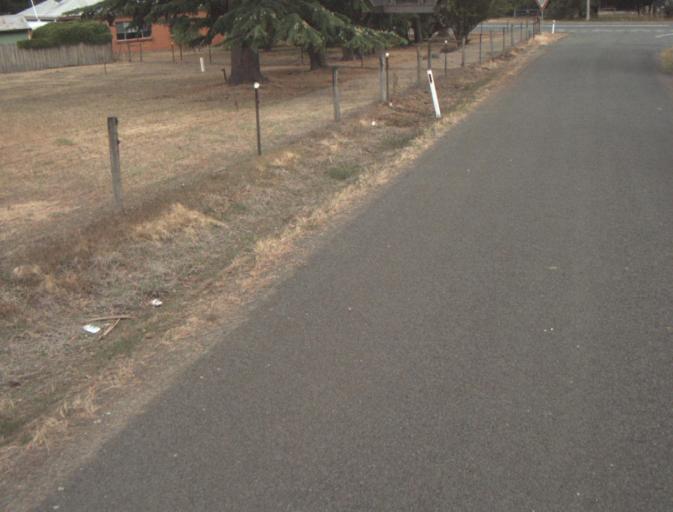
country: AU
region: Tasmania
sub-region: Launceston
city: Mayfield
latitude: -41.2833
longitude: 147.0402
